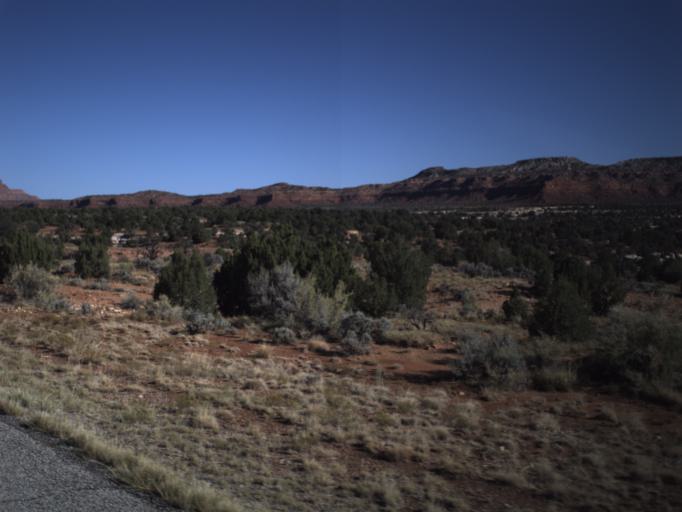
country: US
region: Utah
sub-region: San Juan County
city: Blanding
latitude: 37.6409
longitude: -110.1626
